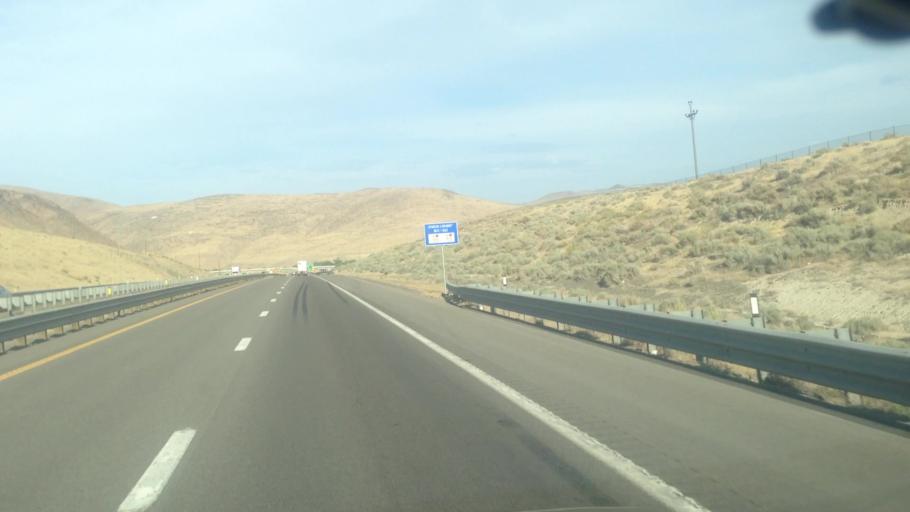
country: US
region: Nevada
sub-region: Washoe County
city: Spanish Springs
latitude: 39.5657
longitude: -119.4985
